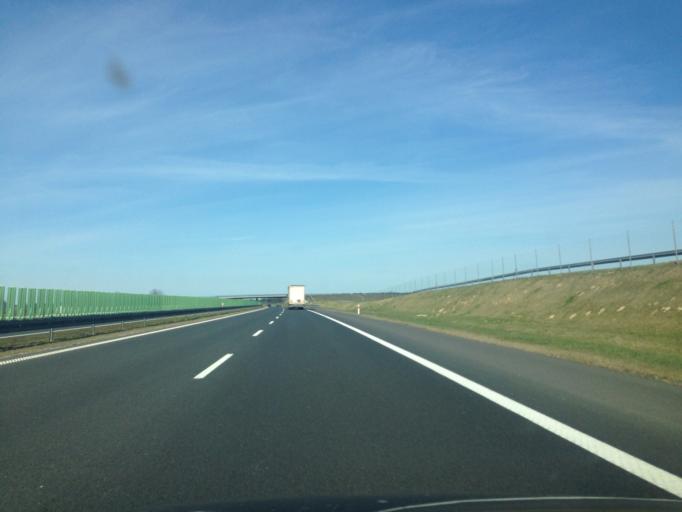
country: PL
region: Pomeranian Voivodeship
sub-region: Powiat starogardzki
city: Smetowo Graniczne
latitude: 53.7555
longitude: 18.6354
